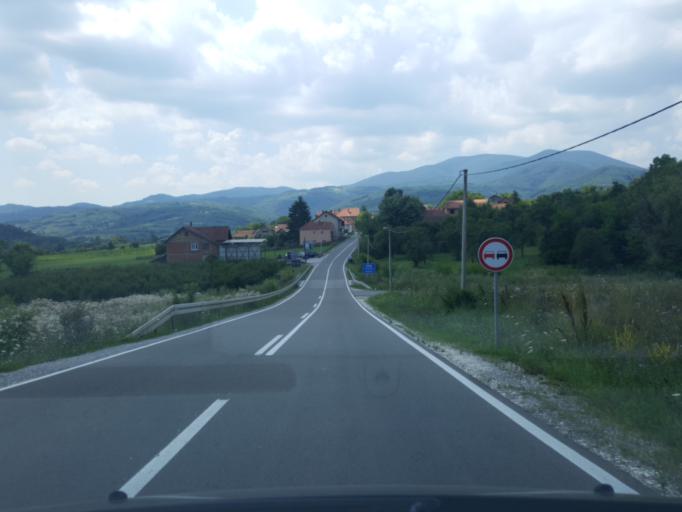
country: RS
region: Central Serbia
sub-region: Sumadijski Okrug
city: Topola
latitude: 44.1989
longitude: 20.6087
